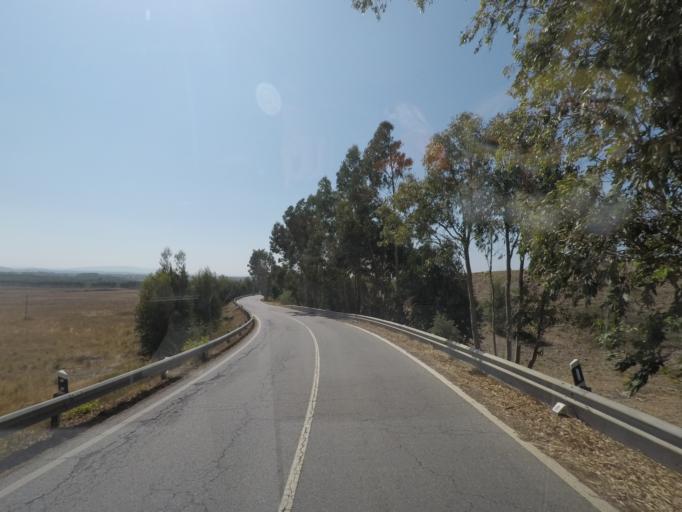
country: PT
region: Beja
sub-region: Odemira
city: Sao Teotonio
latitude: 37.5278
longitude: -8.6999
